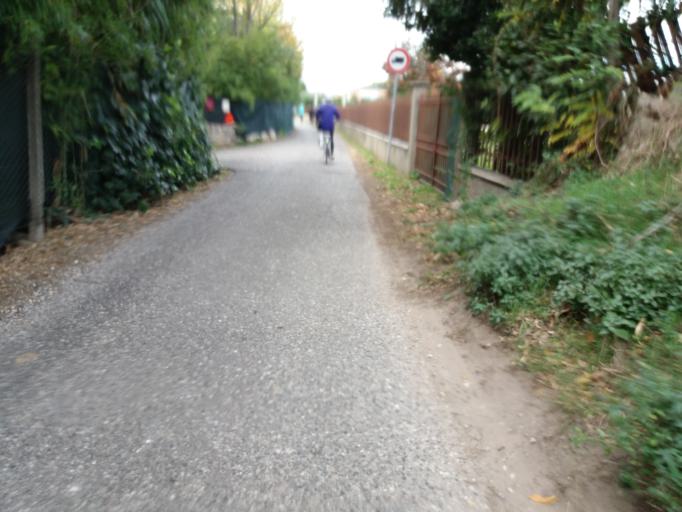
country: IT
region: Veneto
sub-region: Provincia di Verona
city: Calmasino
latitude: 45.5211
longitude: 10.7639
